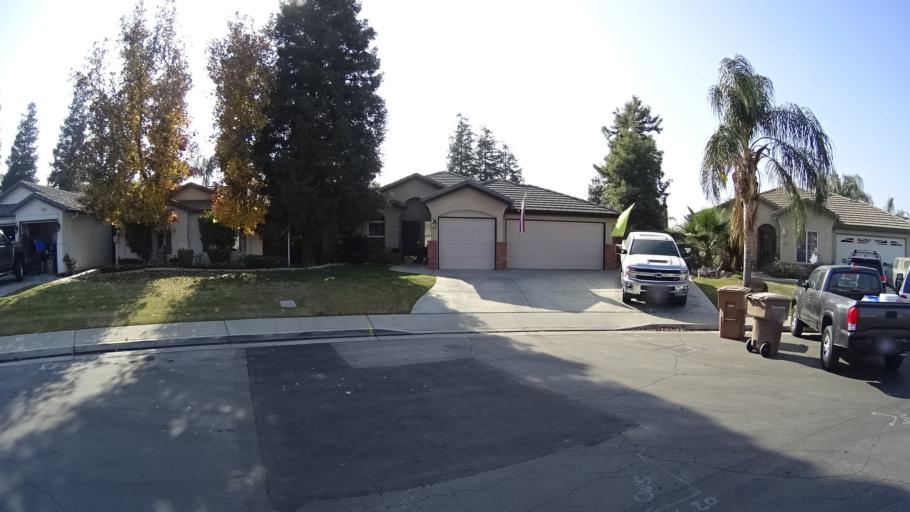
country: US
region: California
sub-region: Kern County
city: Greenacres
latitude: 35.4247
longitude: -119.1150
